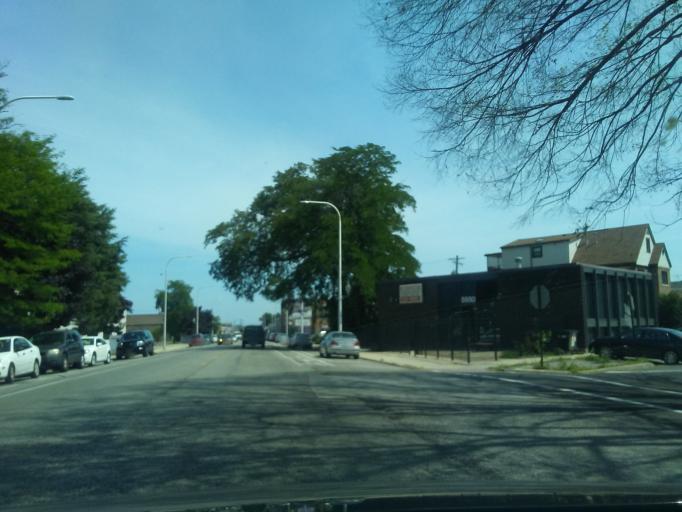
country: US
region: Illinois
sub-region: Cook County
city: Lincolnwood
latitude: 41.9824
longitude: -87.7635
